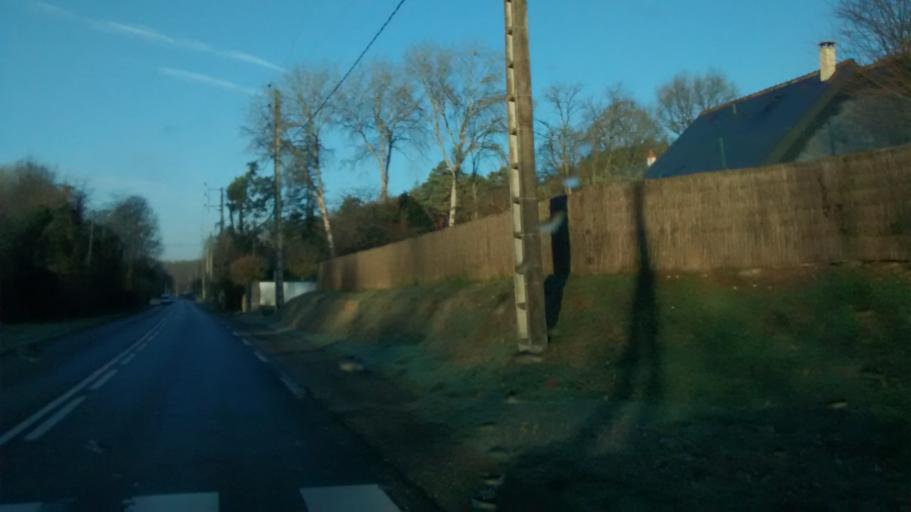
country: FR
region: Centre
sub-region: Departement d'Indre-et-Loire
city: Esvres
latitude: 47.2868
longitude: 0.7718
